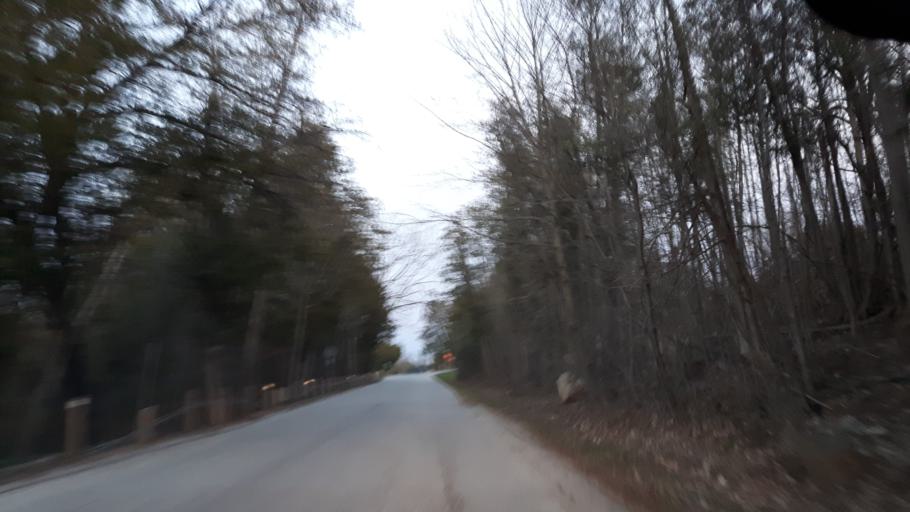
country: CA
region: Ontario
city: Bluewater
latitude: 43.5674
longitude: -81.7006
